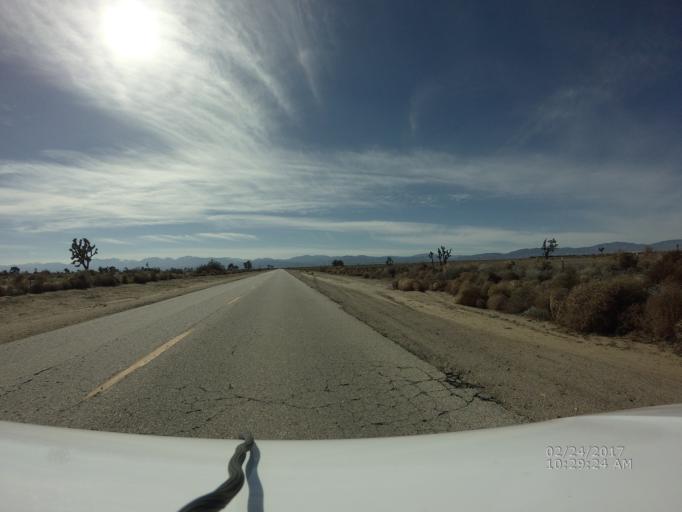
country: US
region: California
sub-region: Los Angeles County
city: Littlerock
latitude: 34.6399
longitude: -118.0053
